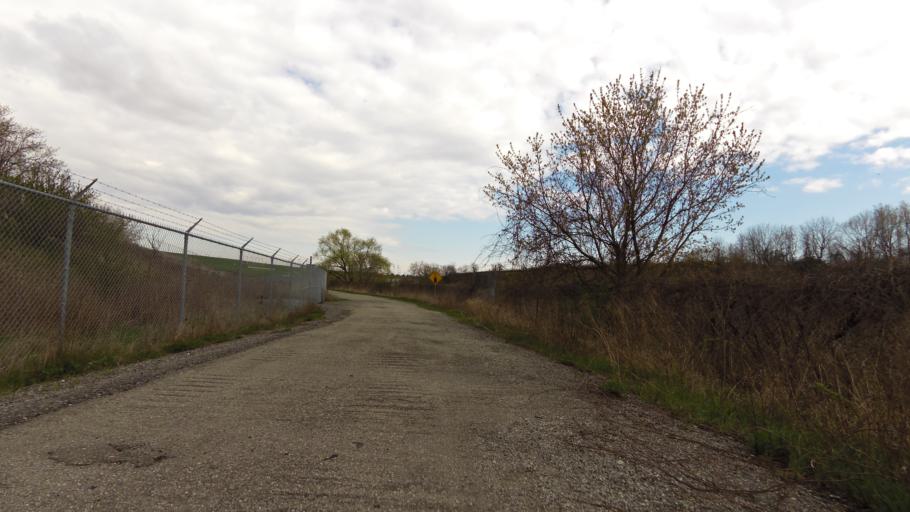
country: CA
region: Ontario
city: Etobicoke
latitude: 43.6609
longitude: -79.6284
